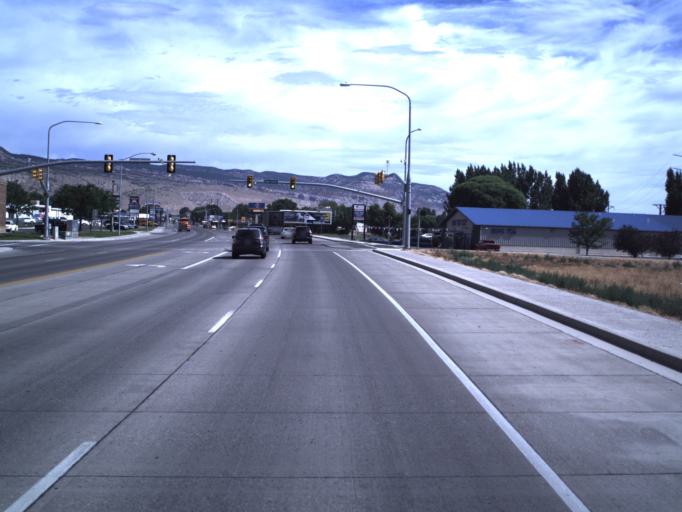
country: US
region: Utah
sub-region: Sevier County
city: Richfield
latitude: 38.7562
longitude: -112.0849
